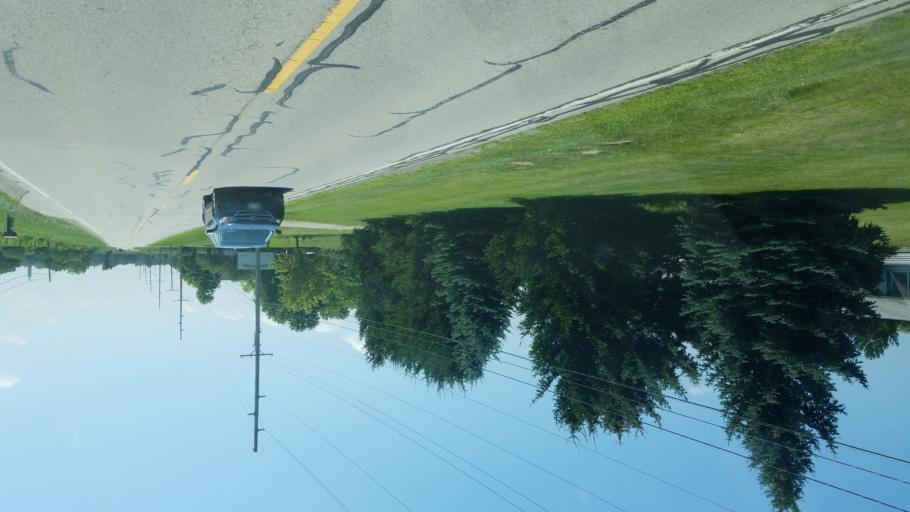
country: US
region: Ohio
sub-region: Huron County
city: Bellevue
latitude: 41.3643
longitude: -82.8271
